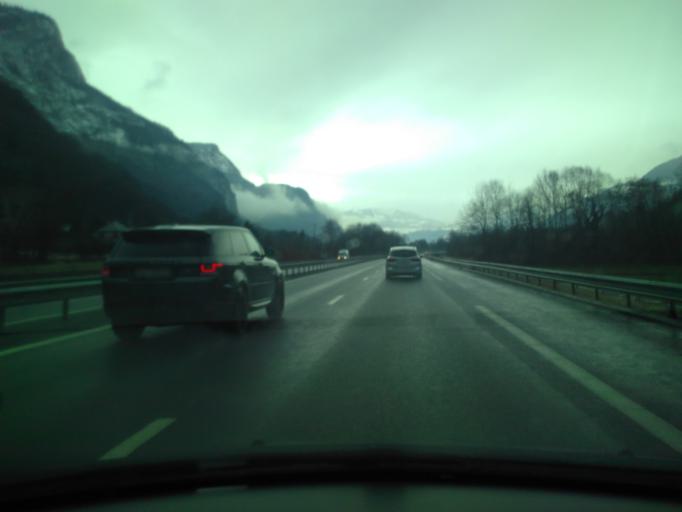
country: FR
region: Rhone-Alpes
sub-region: Departement de la Haute-Savoie
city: Magland
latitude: 45.9949
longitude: 6.6297
